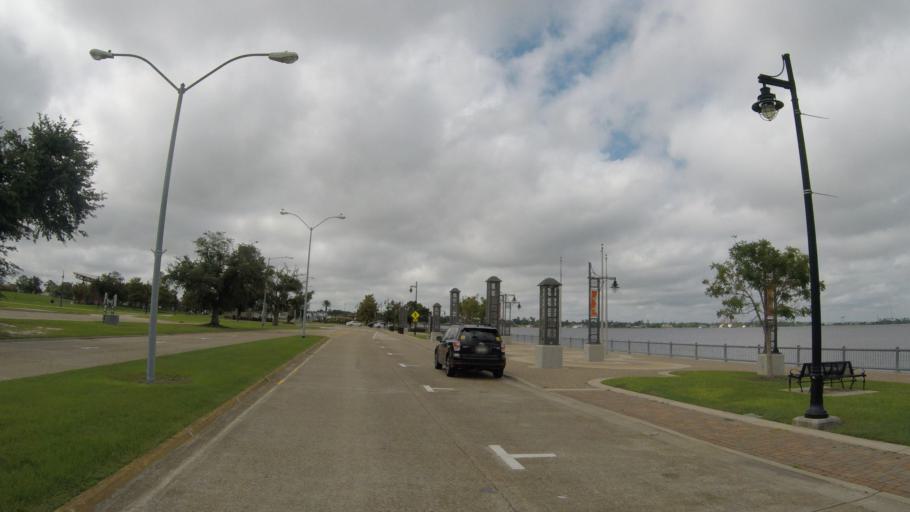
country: US
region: Louisiana
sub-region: Calcasieu Parish
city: Lake Charles
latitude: 30.2270
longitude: -93.2230
